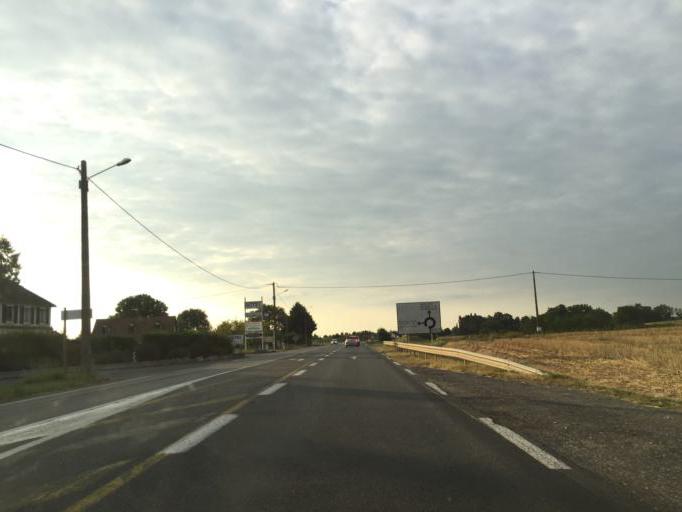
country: FR
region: Auvergne
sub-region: Departement de l'Allier
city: Varennes-sur-Allier
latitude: 46.3538
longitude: 3.3766
